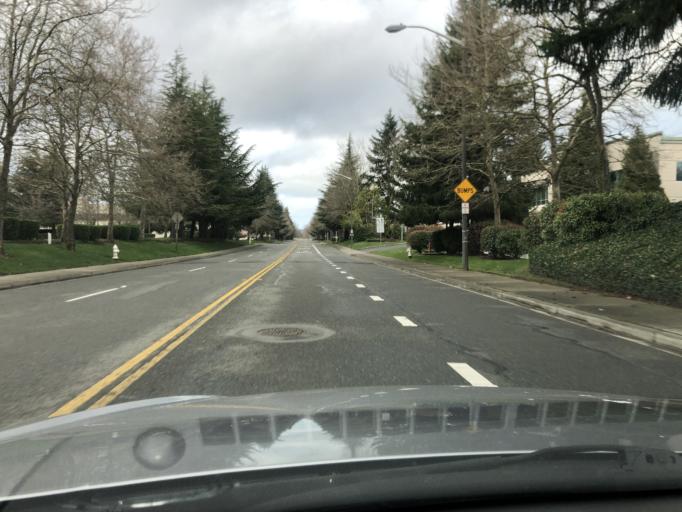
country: US
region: Washington
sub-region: King County
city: Kent
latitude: 47.4181
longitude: -122.2440
